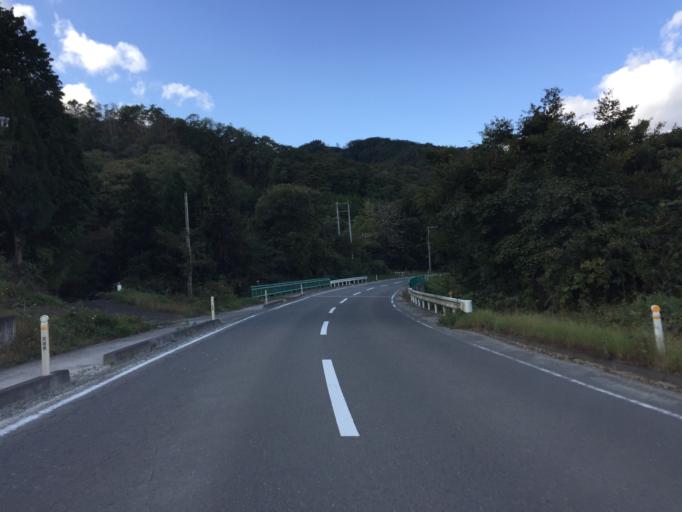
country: JP
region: Miyagi
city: Marumori
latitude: 37.8381
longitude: 140.8300
